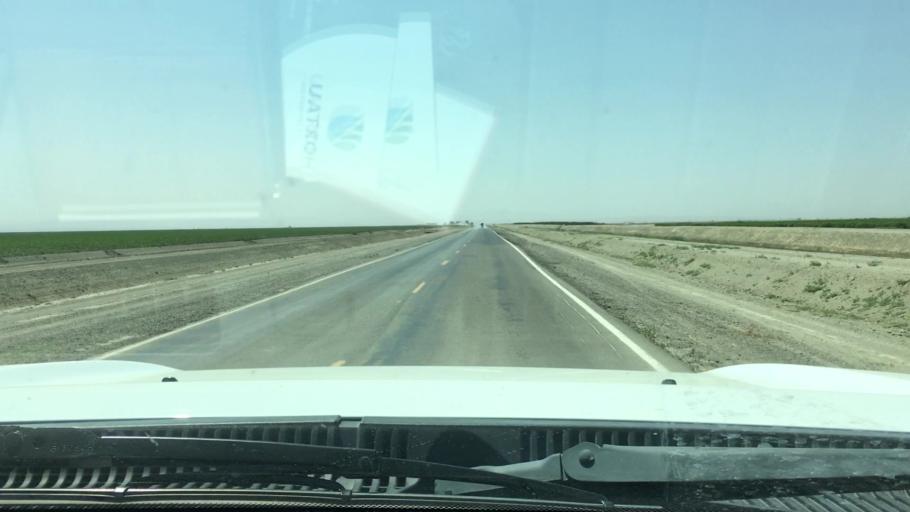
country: US
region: California
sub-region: Tulare County
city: Alpaugh
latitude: 35.9343
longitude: -119.6051
